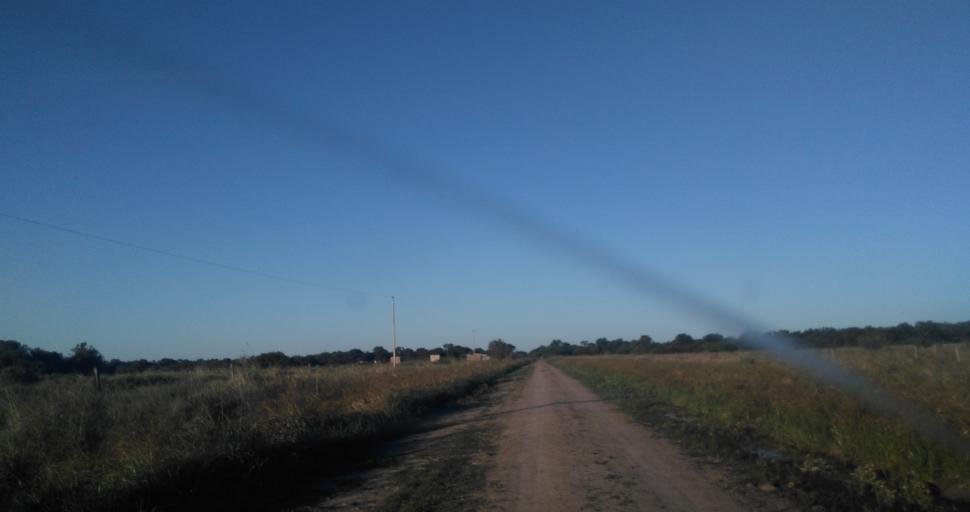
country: AR
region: Chaco
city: Fontana
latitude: -27.3889
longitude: -58.9762
